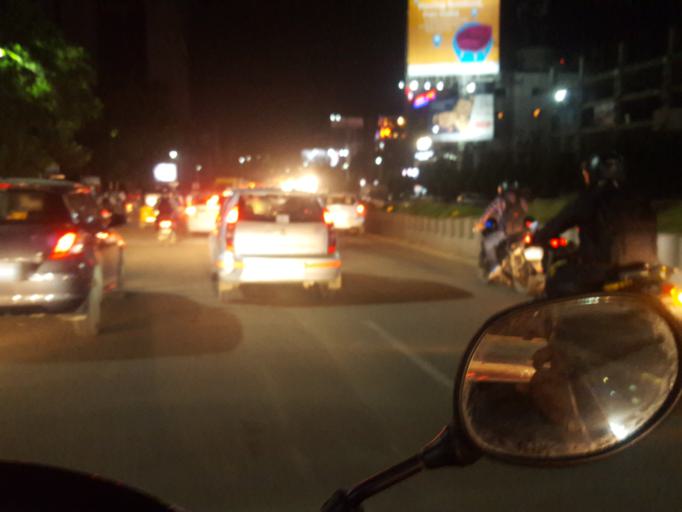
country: IN
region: Telangana
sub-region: Rangareddi
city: Kukatpalli
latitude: 17.4464
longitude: 78.3774
